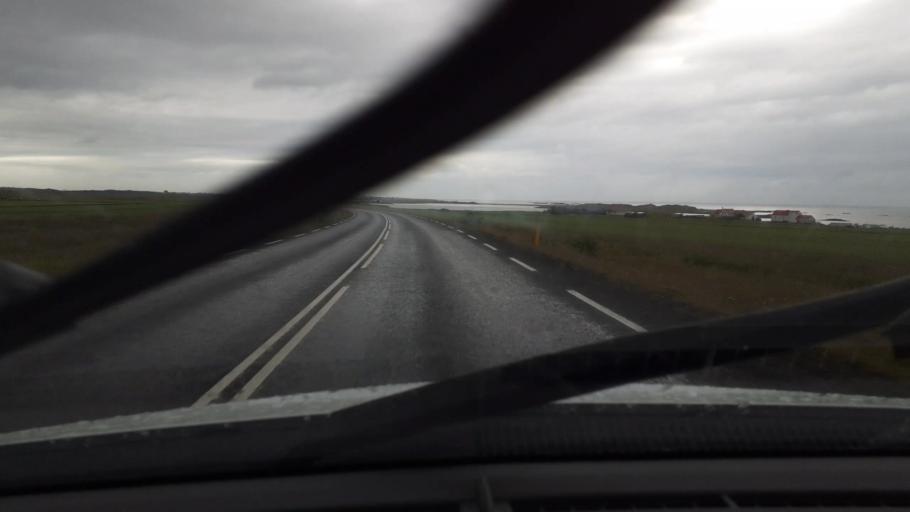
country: IS
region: West
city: Akranes
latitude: 64.3556
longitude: -21.9849
